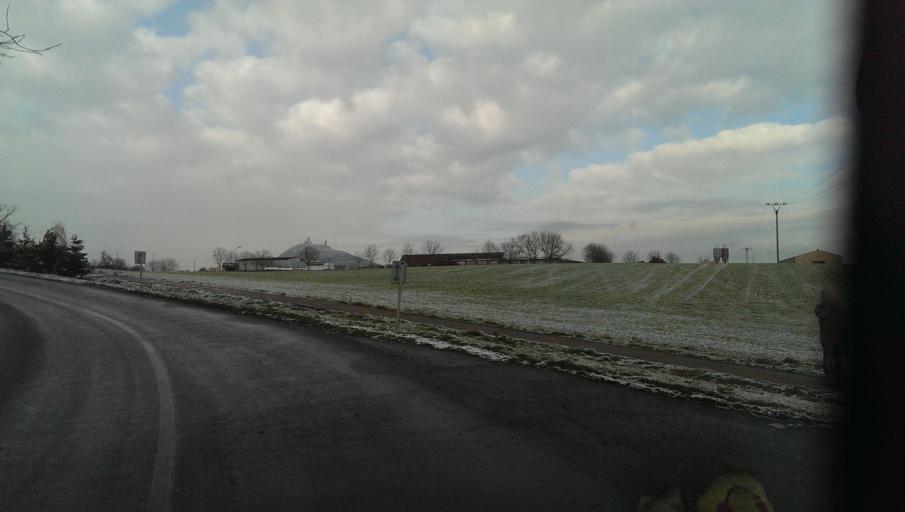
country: CZ
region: Ustecky
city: Libochovice
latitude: 50.4092
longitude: 14.0380
